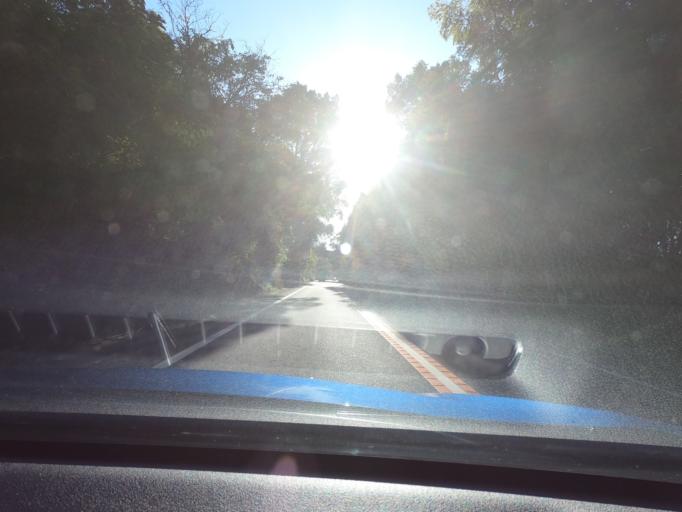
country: JP
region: Kumamoto
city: Minamata
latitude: 32.1690
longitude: 130.3790
